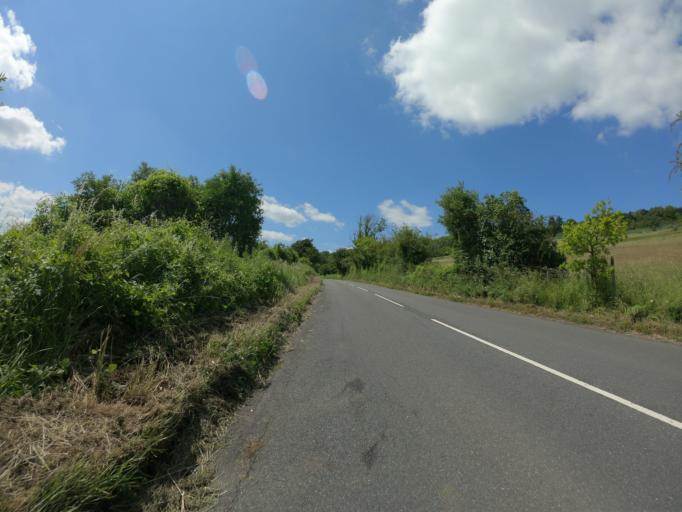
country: GB
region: England
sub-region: Kent
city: Halstead
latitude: 51.3067
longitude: 0.1490
